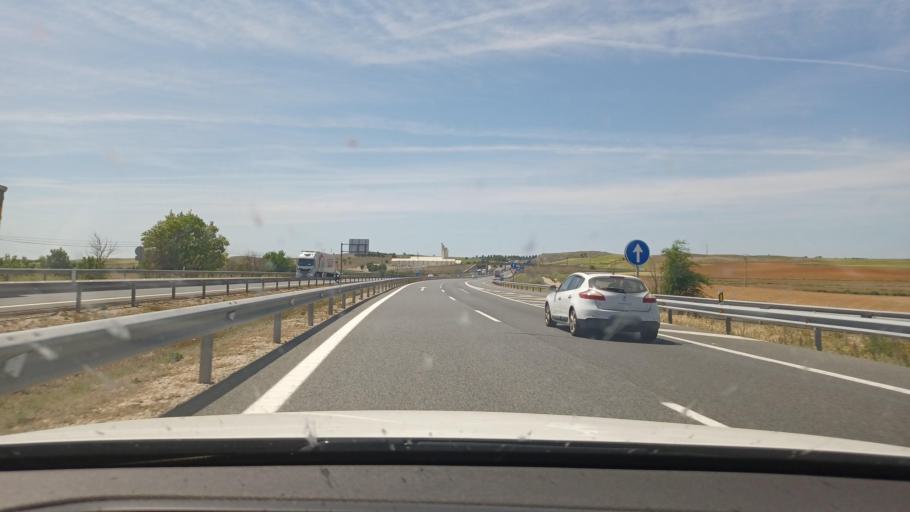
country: ES
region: Castille-La Mancha
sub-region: Provincia de Cuenca
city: Villarrubio
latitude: 39.9512
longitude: -2.9048
